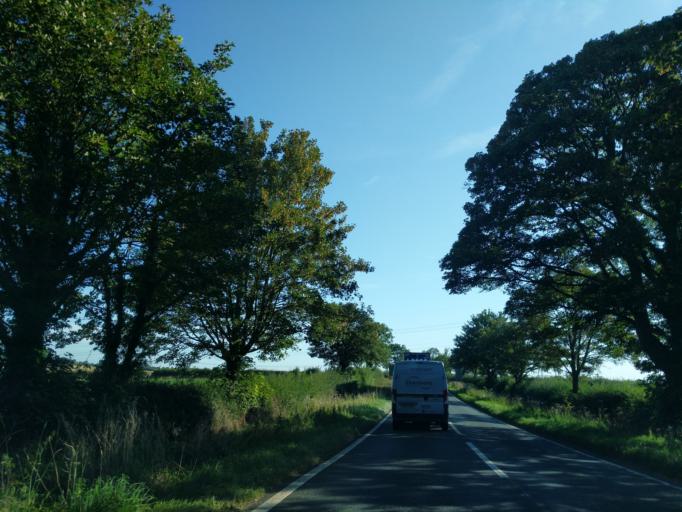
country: GB
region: England
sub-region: District of Rutland
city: Clipsham
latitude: 52.8025
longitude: -0.5533
